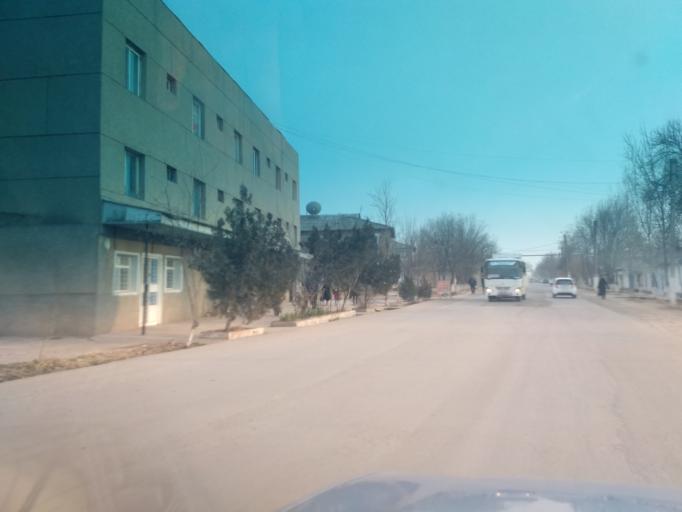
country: UZ
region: Sirdaryo
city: Guliston
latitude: 40.4931
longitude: 68.7870
